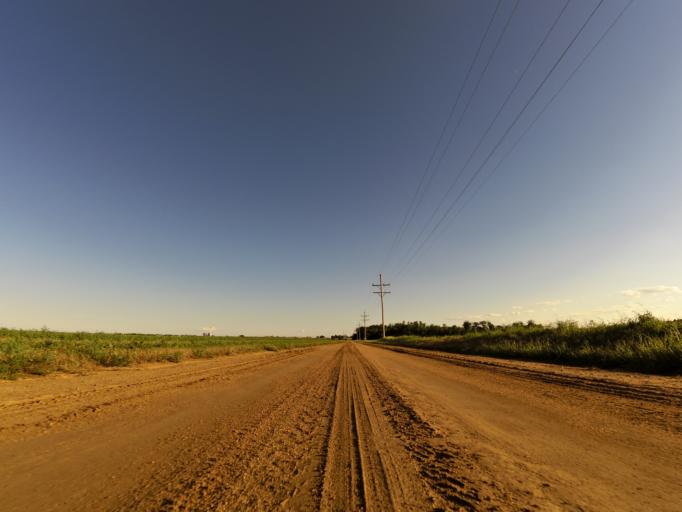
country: US
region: Kansas
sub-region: Reno County
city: South Hutchinson
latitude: 38.0088
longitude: -98.0319
